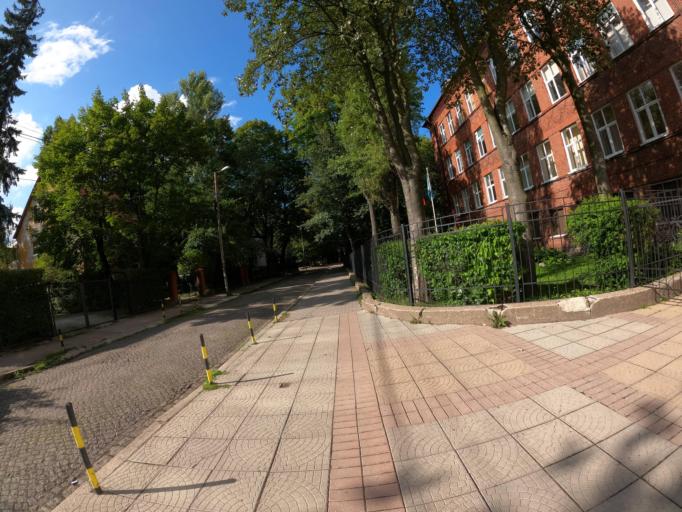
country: RU
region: Kaliningrad
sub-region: Gorod Kaliningrad
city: Kaliningrad
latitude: 54.7293
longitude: 20.4693
